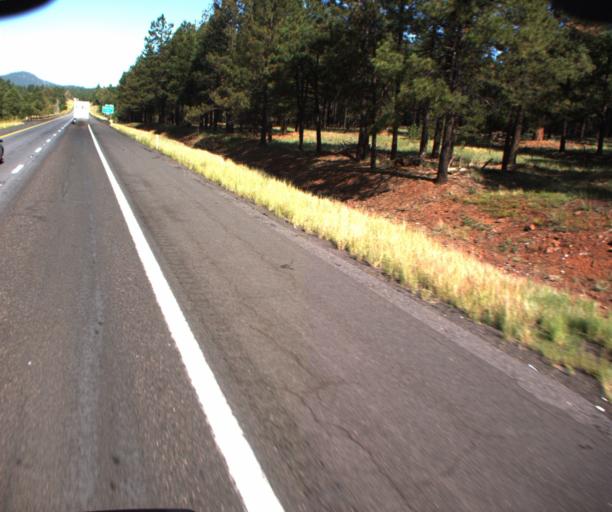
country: US
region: Arizona
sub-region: Coconino County
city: Parks
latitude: 35.2543
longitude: -111.9141
